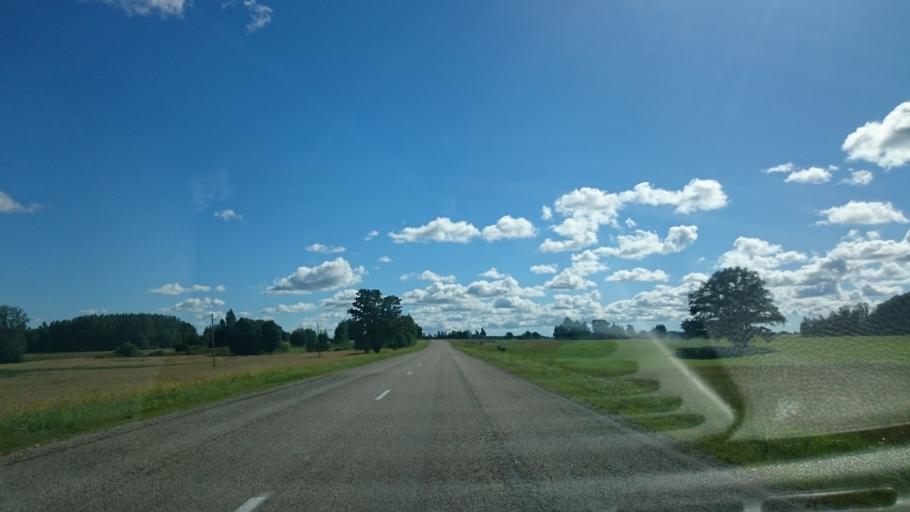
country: LV
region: Aizpute
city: Aizpute
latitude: 56.7692
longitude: 21.6240
